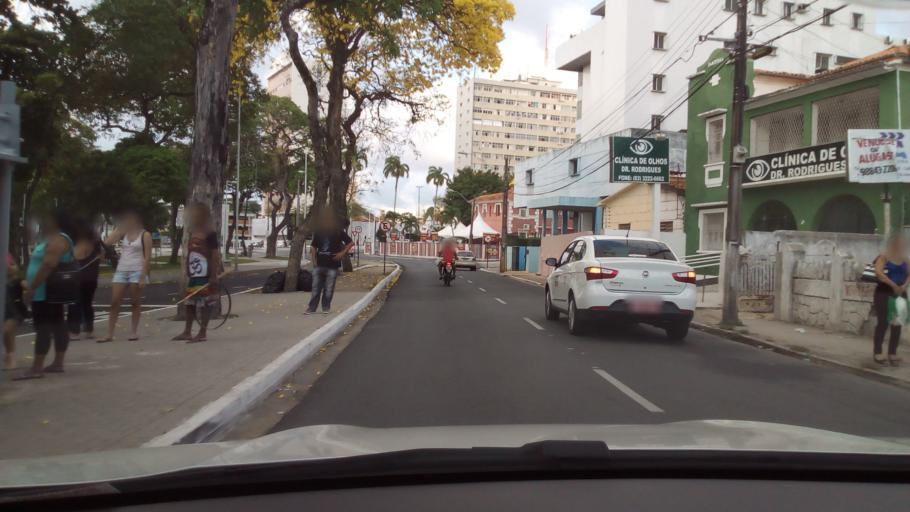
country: BR
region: Paraiba
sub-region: Joao Pessoa
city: Joao Pessoa
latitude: -7.1217
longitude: -34.8788
